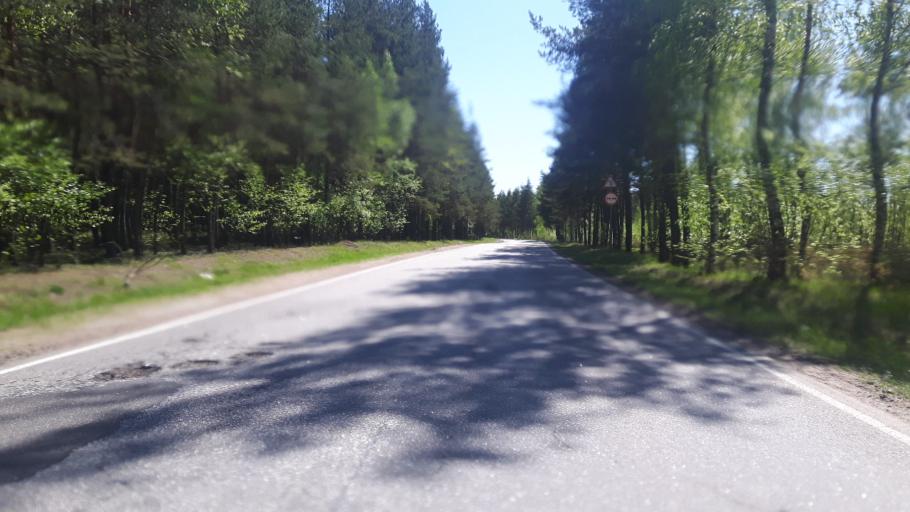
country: RU
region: Leningrad
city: Glebychevo
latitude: 60.3498
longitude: 28.8176
